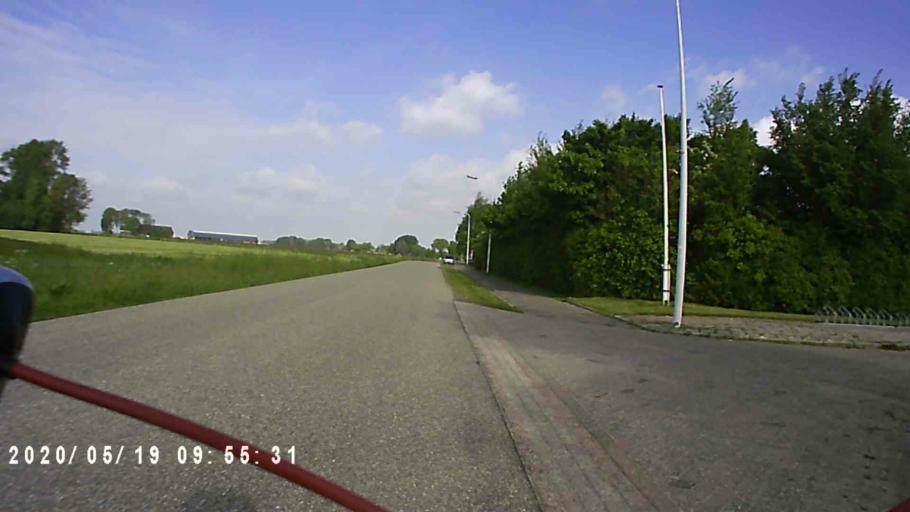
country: NL
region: Groningen
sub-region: Gemeente Zuidhorn
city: Grijpskerk
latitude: 53.2908
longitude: 6.2469
